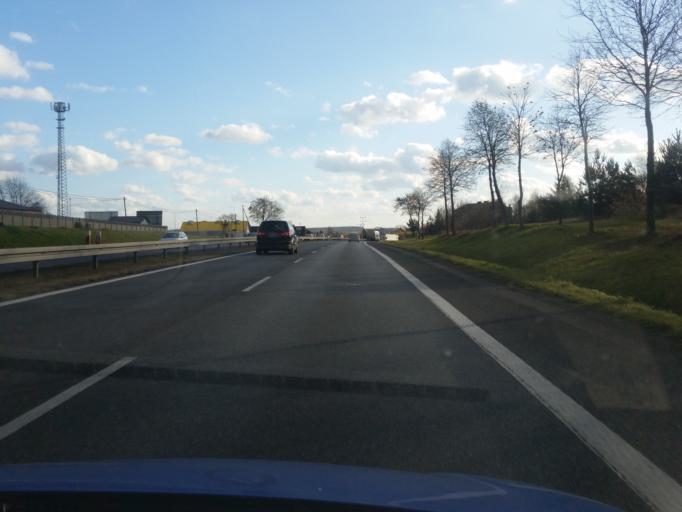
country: PL
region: Silesian Voivodeship
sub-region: Powiat myszkowski
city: Kozieglowy
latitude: 50.6100
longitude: 19.1538
